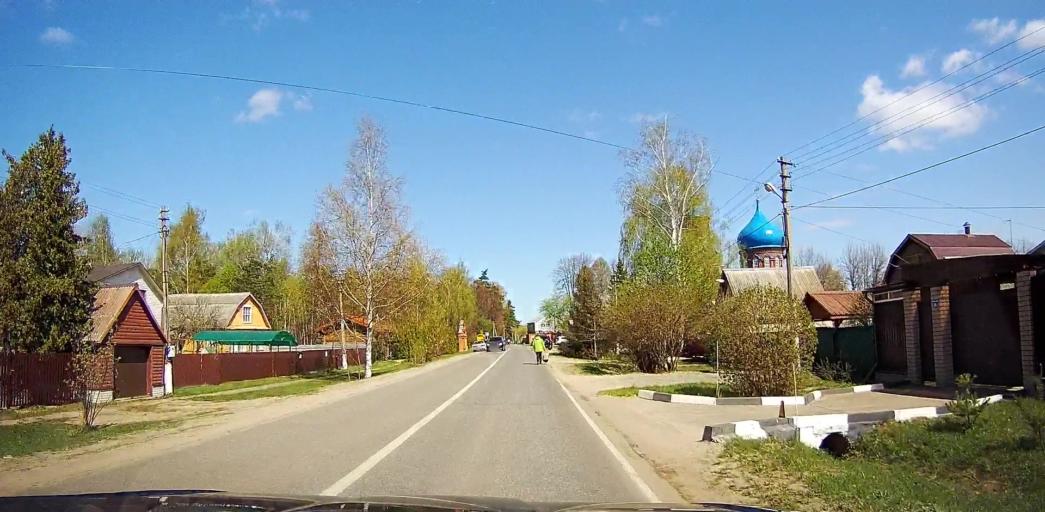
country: RU
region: Moskovskaya
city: Gzhel'
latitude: 55.6254
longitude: 38.3027
